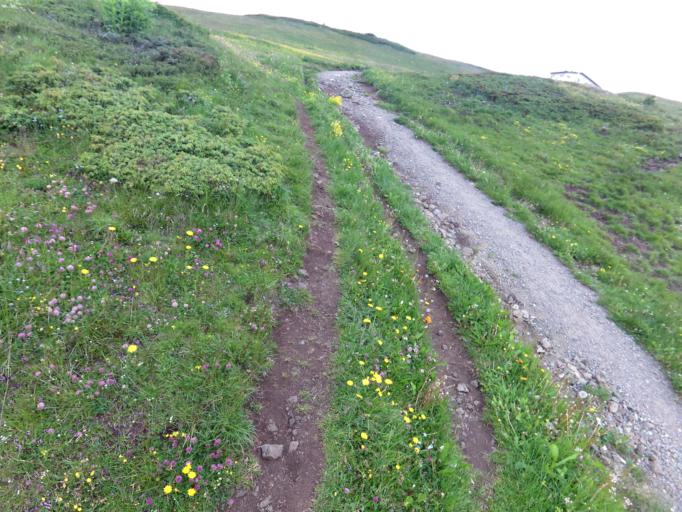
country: IT
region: Trentino-Alto Adige
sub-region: Bolzano
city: Castelrotto
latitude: 46.5499
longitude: 11.6151
